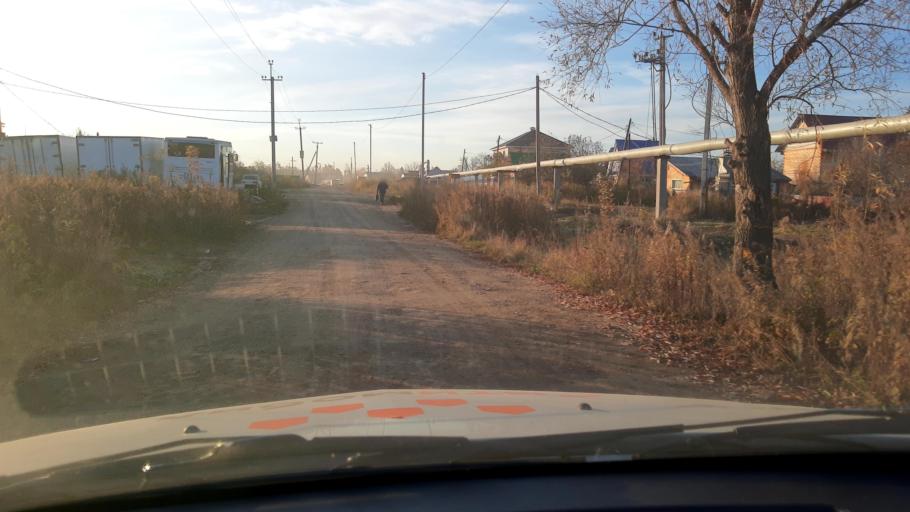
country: RU
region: Bashkortostan
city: Ufa
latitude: 54.8157
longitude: 56.1545
